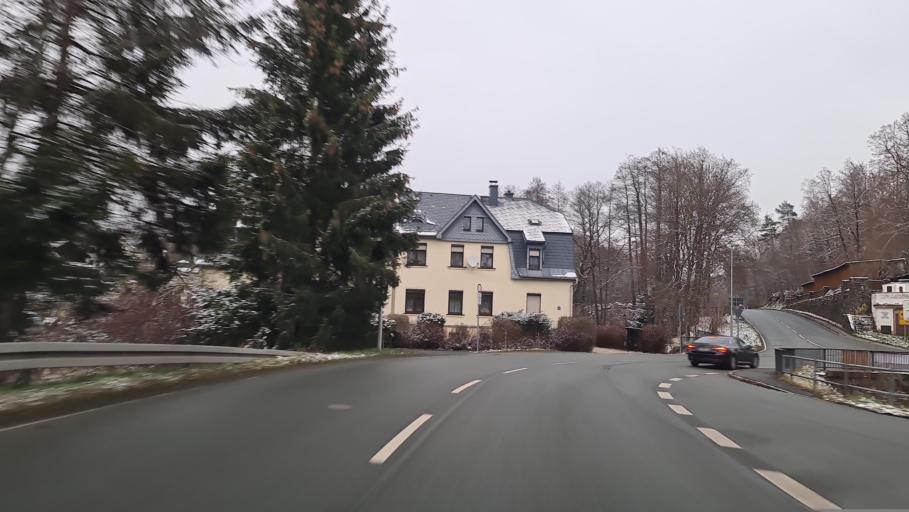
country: DE
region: Saxony
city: Markneukirchen
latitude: 50.3094
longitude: 12.3065
